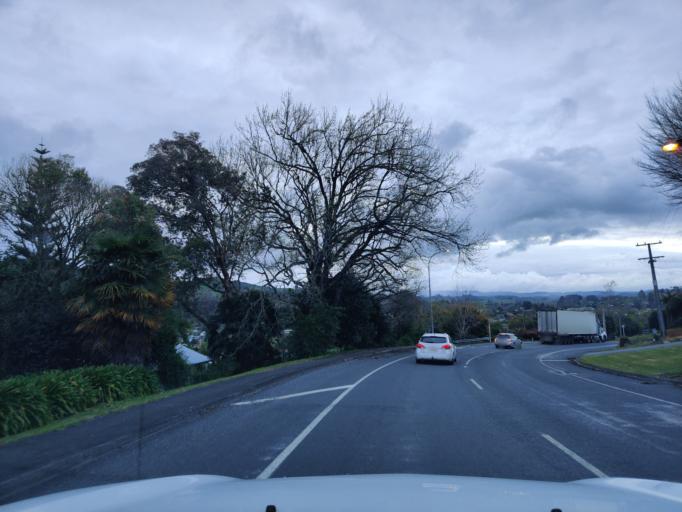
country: NZ
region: Waikato
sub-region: Otorohanga District
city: Otorohanga
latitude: -38.3437
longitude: 175.1674
